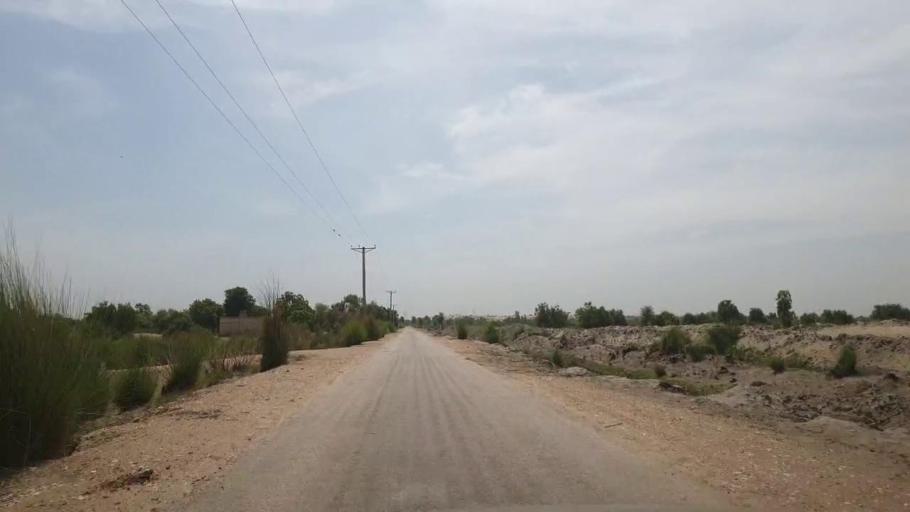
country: PK
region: Sindh
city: Kot Diji
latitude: 27.1140
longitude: 69.0149
